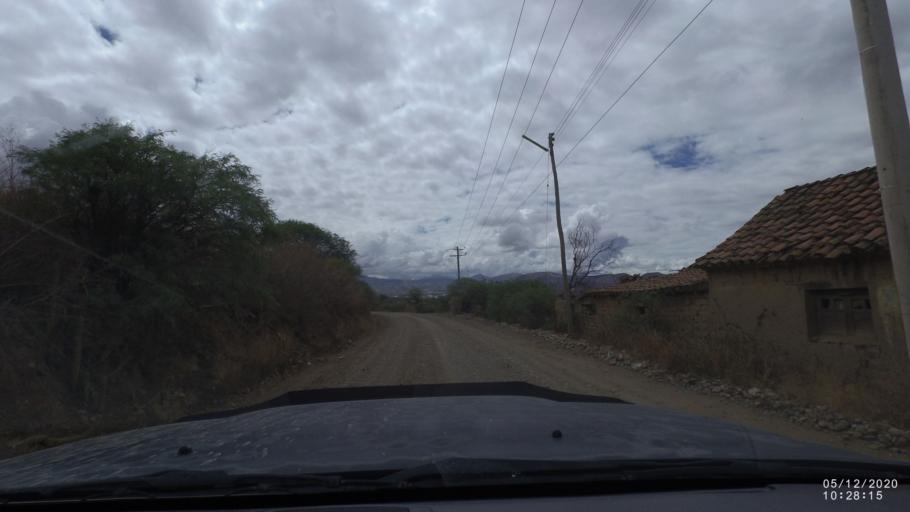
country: BO
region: Cochabamba
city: Sipe Sipe
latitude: -17.5372
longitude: -66.2750
